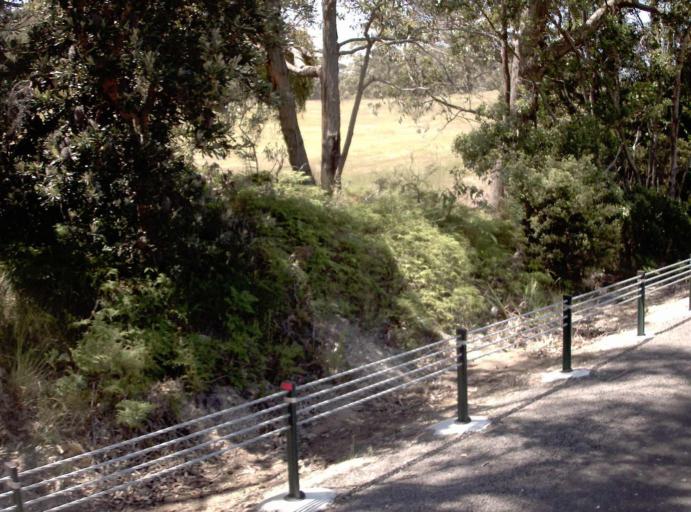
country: AU
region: Victoria
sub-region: East Gippsland
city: Lakes Entrance
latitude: -37.7080
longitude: 148.6986
